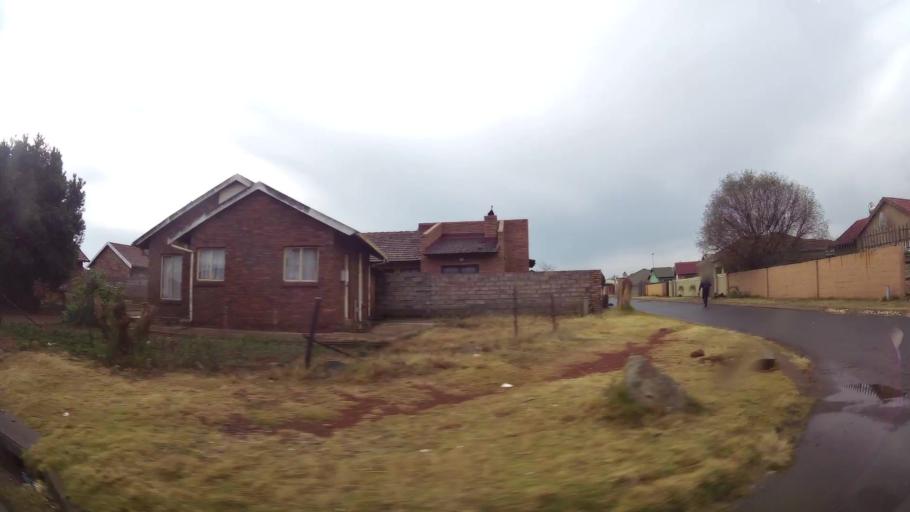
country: ZA
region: Gauteng
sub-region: Ekurhuleni Metropolitan Municipality
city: Germiston
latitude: -26.3268
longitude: 28.1908
